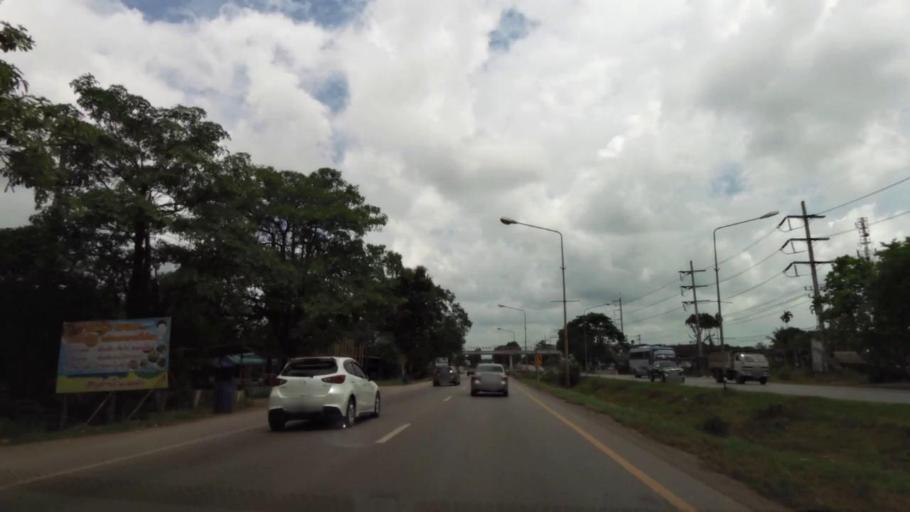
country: TH
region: Chanthaburi
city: Na Yai Am
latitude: 12.7844
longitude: 101.7953
